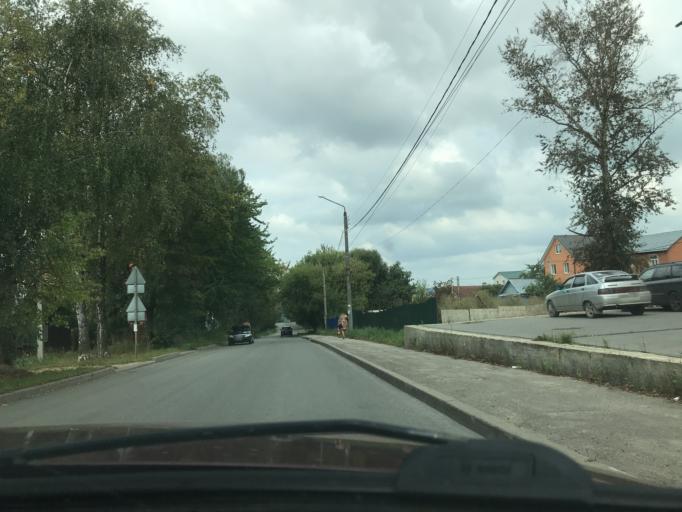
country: RU
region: Kaluga
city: Kaluga
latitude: 54.5345
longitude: 36.2523
